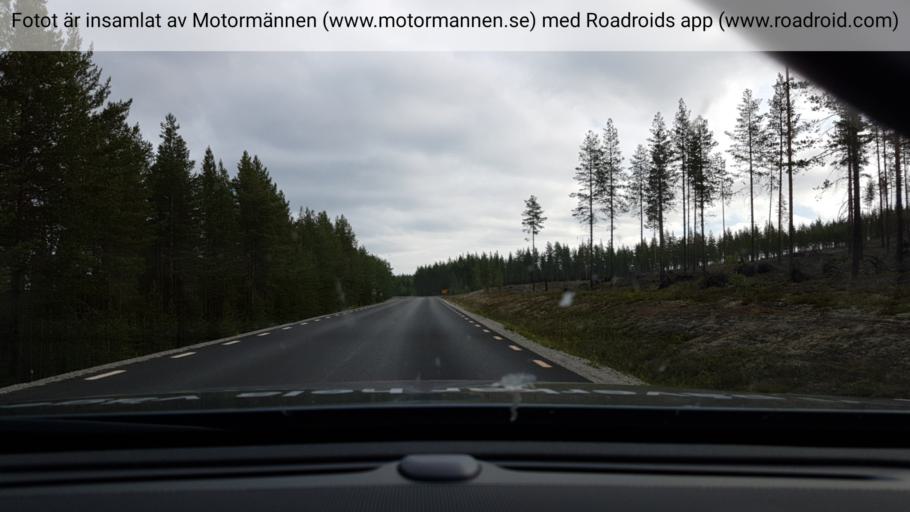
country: SE
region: Vaesterbotten
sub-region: Norsjo Kommun
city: Norsjoe
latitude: 64.5026
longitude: 19.3292
